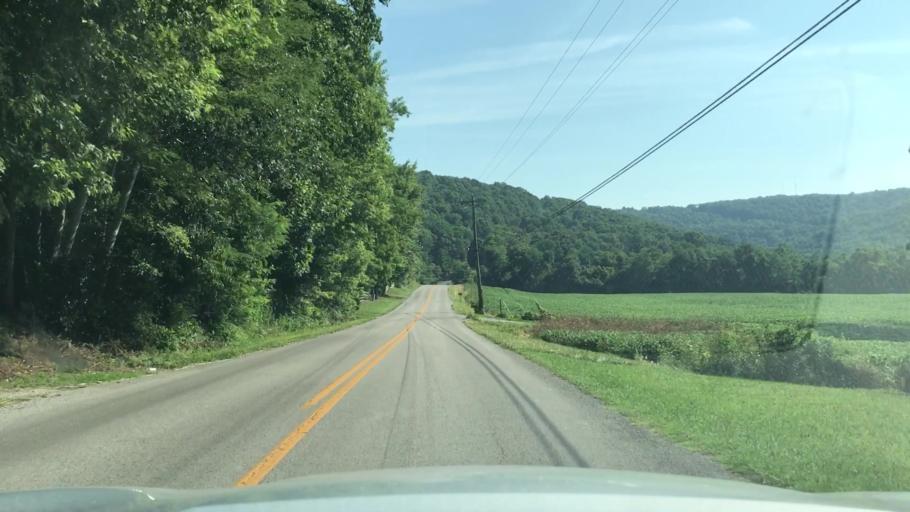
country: US
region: Kentucky
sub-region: Clinton County
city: Albany
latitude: 36.7066
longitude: -85.0343
